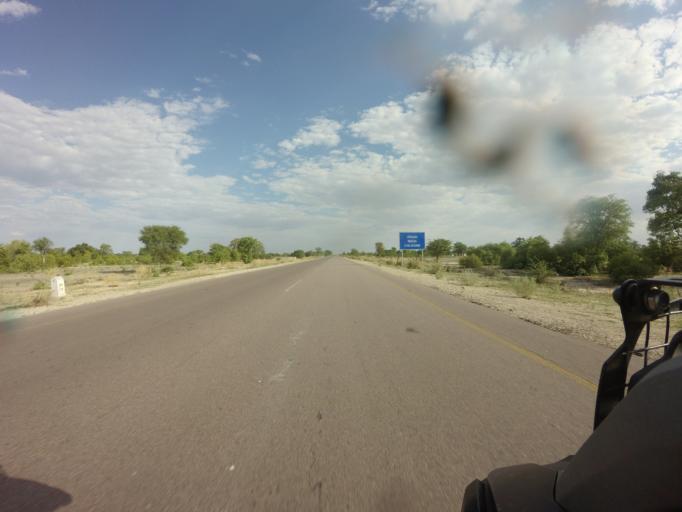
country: AO
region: Cunene
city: Ondjiva
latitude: -17.0229
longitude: 15.6576
